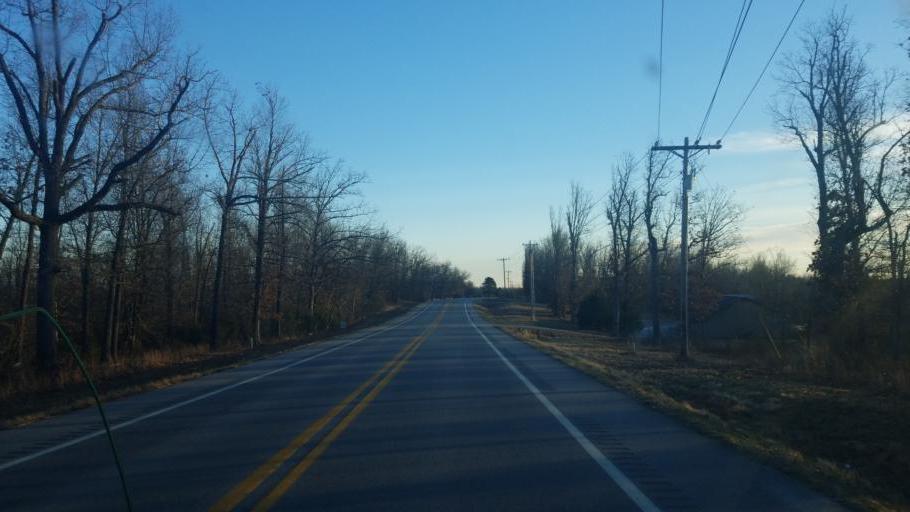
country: US
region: Arkansas
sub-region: Baxter County
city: Mountain Home
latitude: 36.3818
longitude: -92.1525
